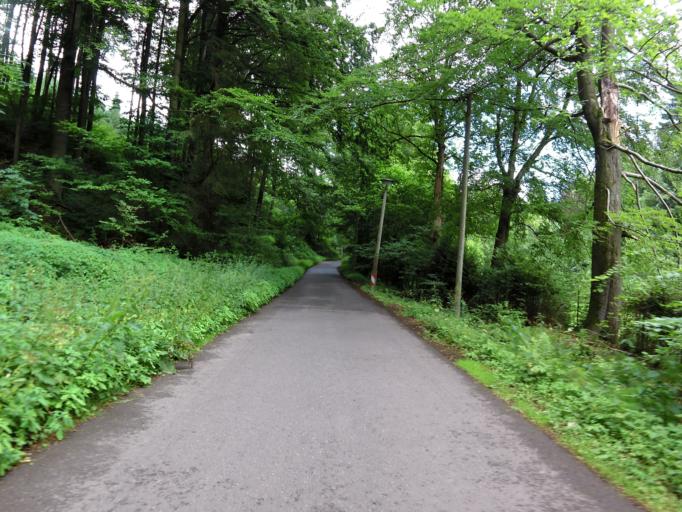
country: DE
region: Thuringia
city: Tabarz
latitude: 50.8624
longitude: 10.5069
